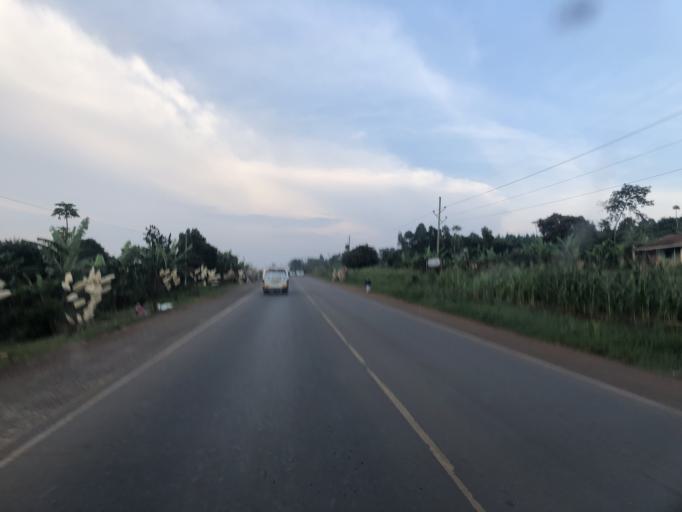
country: UG
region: Central Region
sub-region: Mpigi District
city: Mpigi
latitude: 0.2296
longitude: 32.3448
